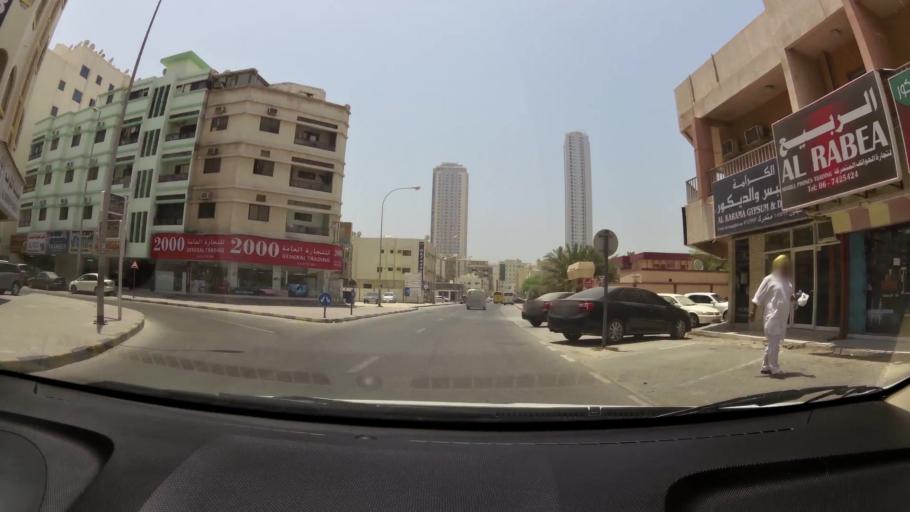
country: AE
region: Ajman
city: Ajman
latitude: 25.4079
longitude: 55.4383
